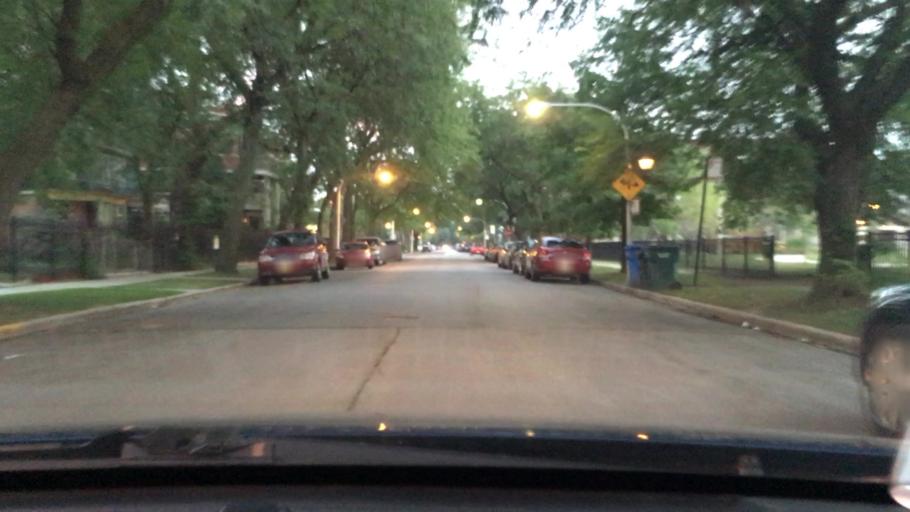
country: US
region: Illinois
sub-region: Cook County
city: Chicago
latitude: 41.8123
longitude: -87.5993
